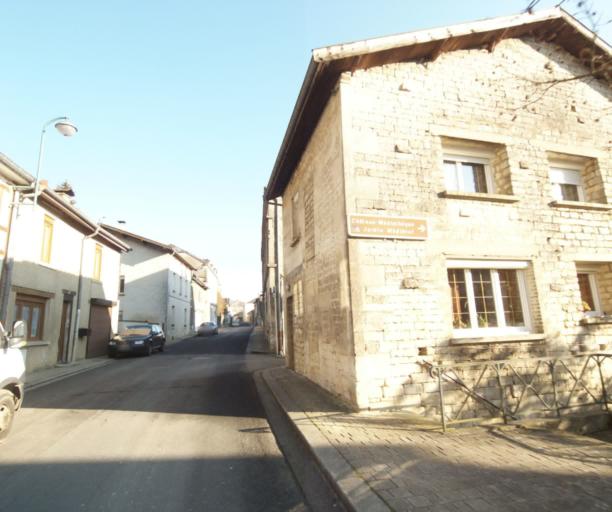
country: FR
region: Champagne-Ardenne
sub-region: Departement de la Haute-Marne
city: Chevillon
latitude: 48.5289
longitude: 5.1302
